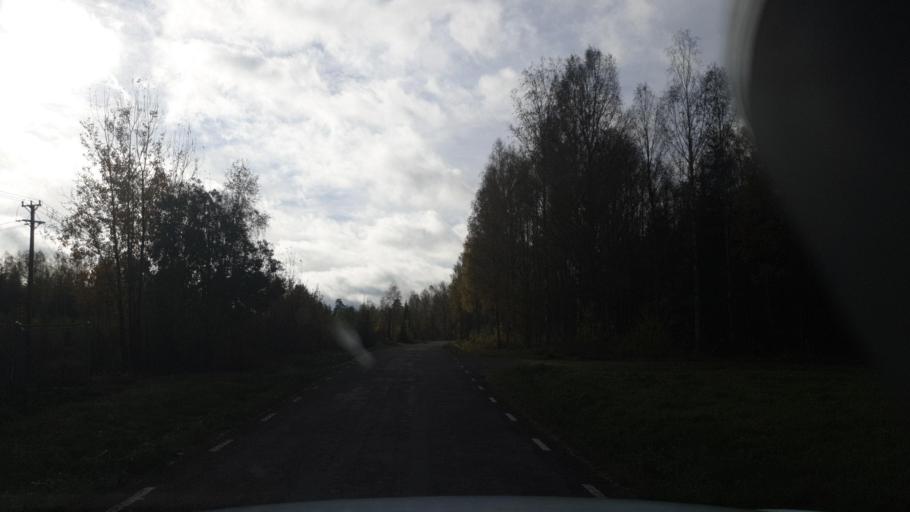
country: SE
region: Vaermland
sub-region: Sunne Kommun
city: Sunne
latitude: 59.6239
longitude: 12.9590
